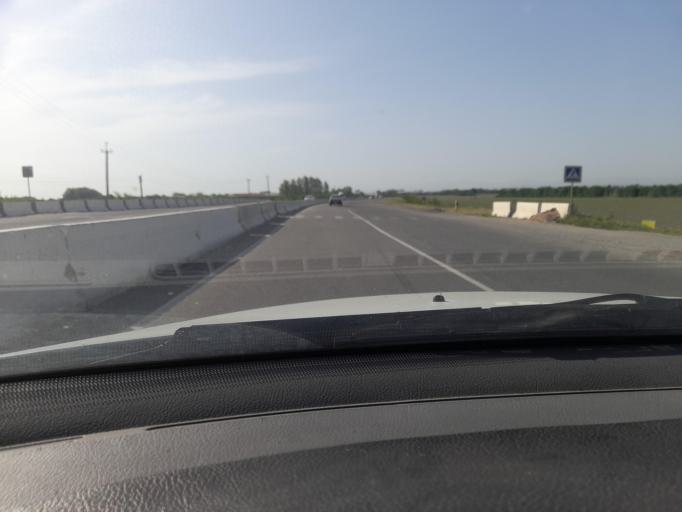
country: UZ
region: Samarqand
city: Kattaqo'rg'on
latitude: 39.9250
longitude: 66.2744
